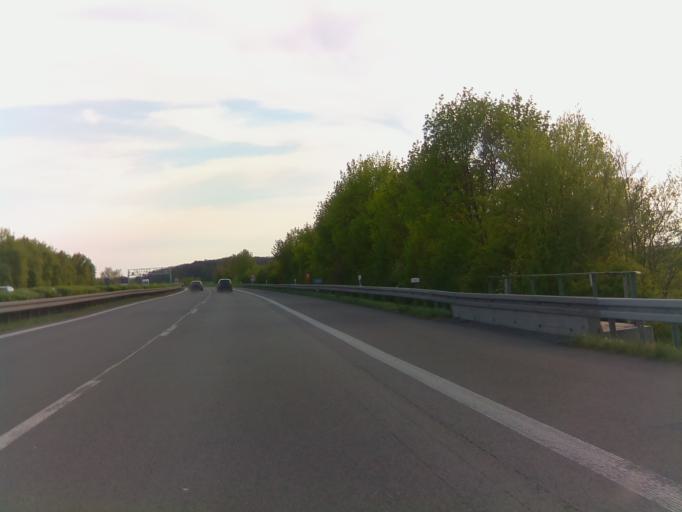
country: DE
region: Bavaria
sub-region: Regierungsbezirk Unterfranken
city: Kleinrinderfeld
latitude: 49.7016
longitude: 9.7965
